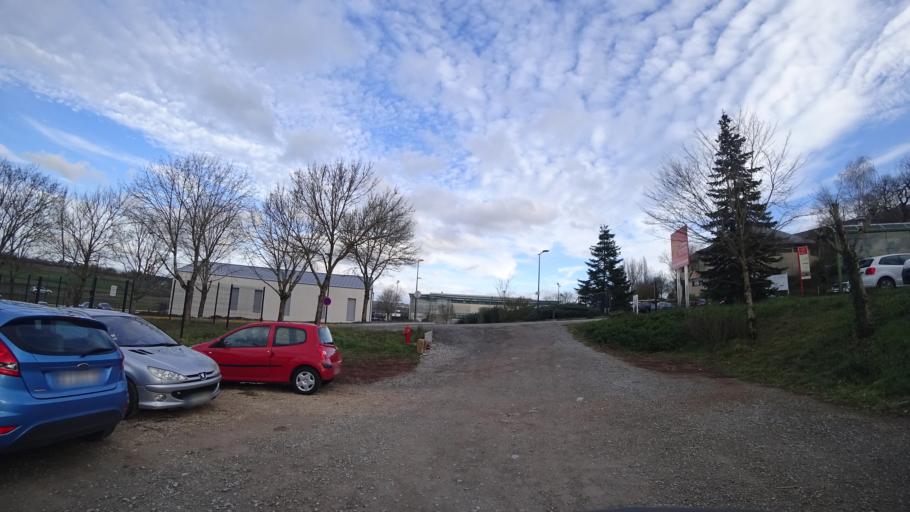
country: FR
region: Midi-Pyrenees
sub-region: Departement de l'Aveyron
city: Sebazac-Concoures
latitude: 44.3831
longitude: 2.5854
